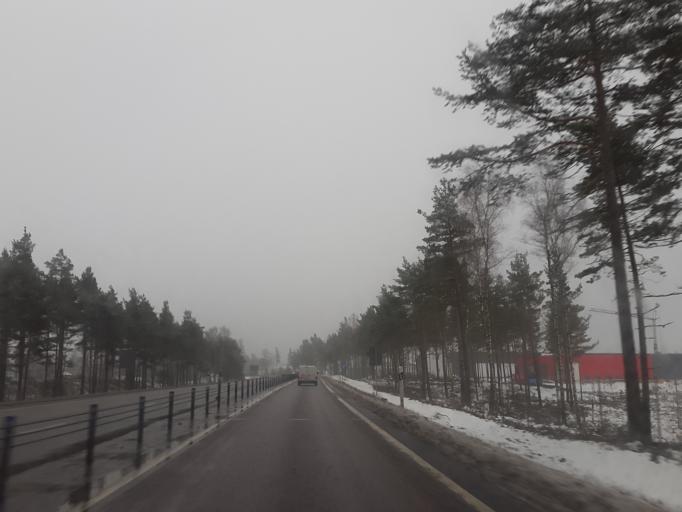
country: SE
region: Joenkoeping
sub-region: Jonkopings Kommun
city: Jonkoping
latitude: 57.7705
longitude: 14.0849
